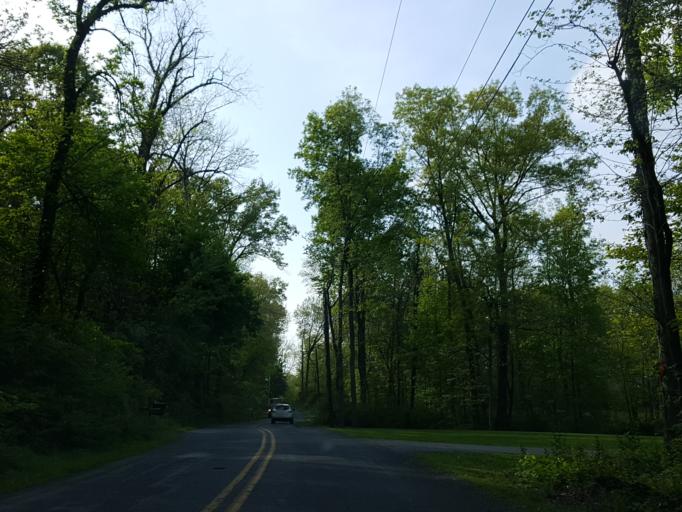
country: US
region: Pennsylvania
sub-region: Lancaster County
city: Elizabethtown
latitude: 40.1900
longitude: -76.5638
